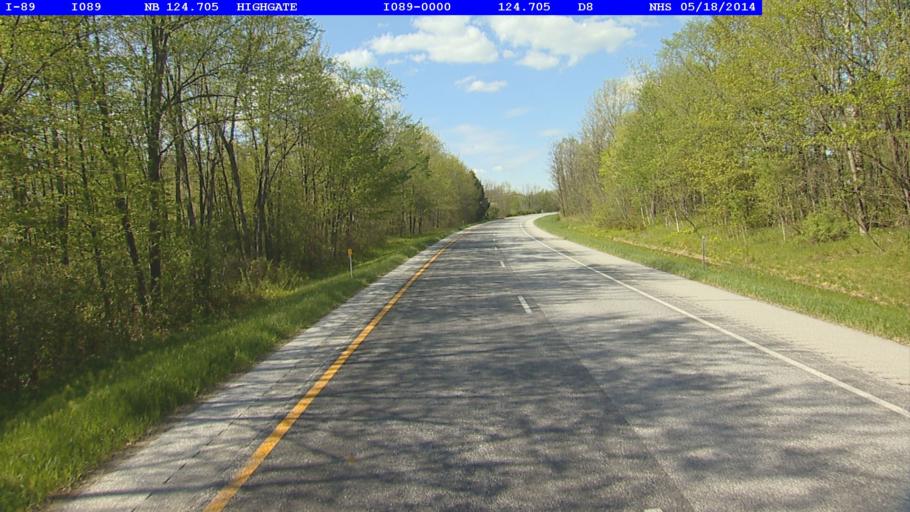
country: US
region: Vermont
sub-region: Franklin County
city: Swanton
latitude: 44.9406
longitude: -73.1147
